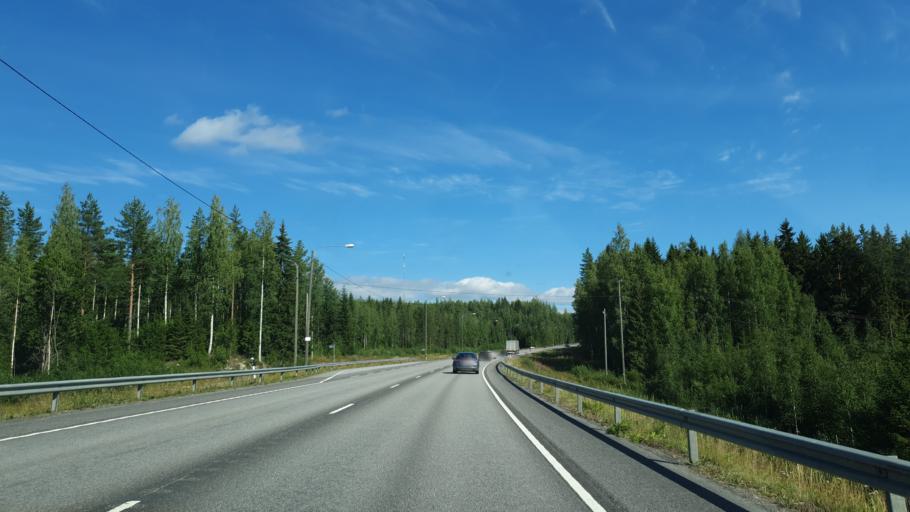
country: FI
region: Central Finland
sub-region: Jyvaeskylae
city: Toivakka
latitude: 62.2485
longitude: 26.0209
